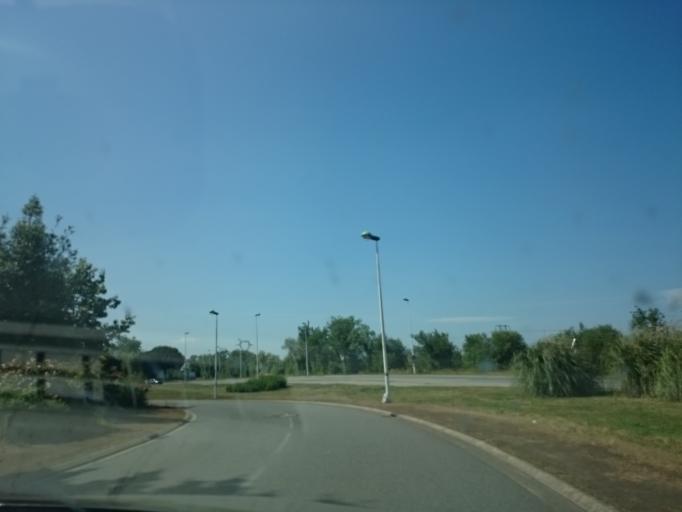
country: FR
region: Pays de la Loire
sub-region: Departement de la Loire-Atlantique
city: Indre
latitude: 47.2034
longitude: -1.6740
